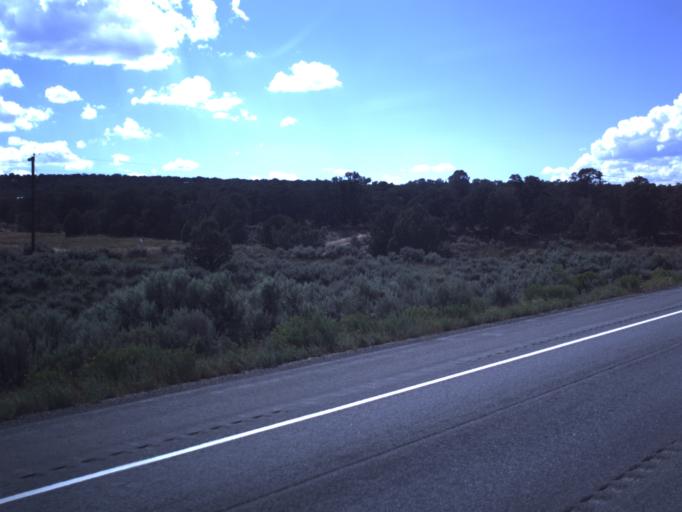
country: US
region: Utah
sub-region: Duchesne County
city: Duchesne
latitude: 40.1940
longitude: -110.6853
